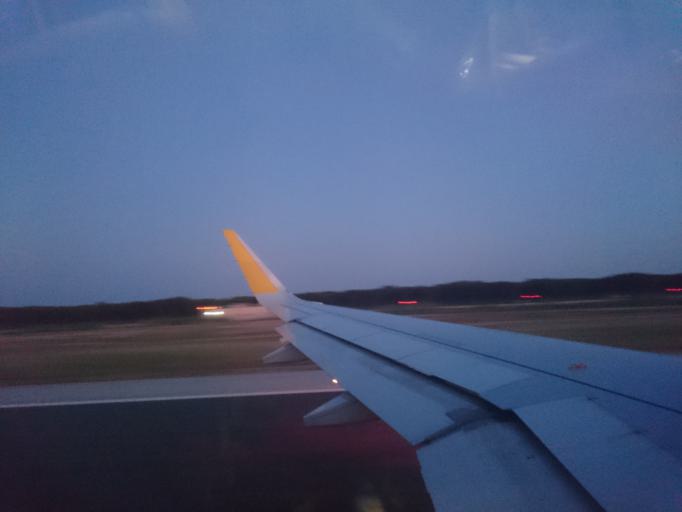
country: ES
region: Catalonia
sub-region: Provincia de Barcelona
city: El Prat de Llobregat
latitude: 41.2903
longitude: 2.0977
